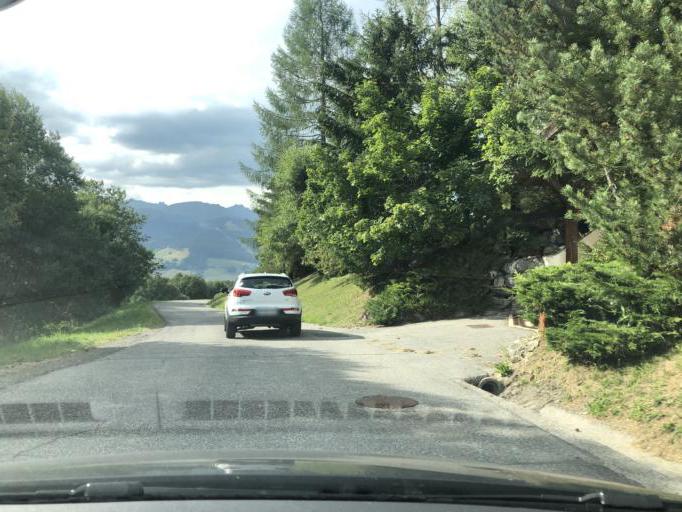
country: FR
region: Rhone-Alpes
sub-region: Departement de la Haute-Savoie
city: Megeve
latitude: 45.8378
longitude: 6.6450
